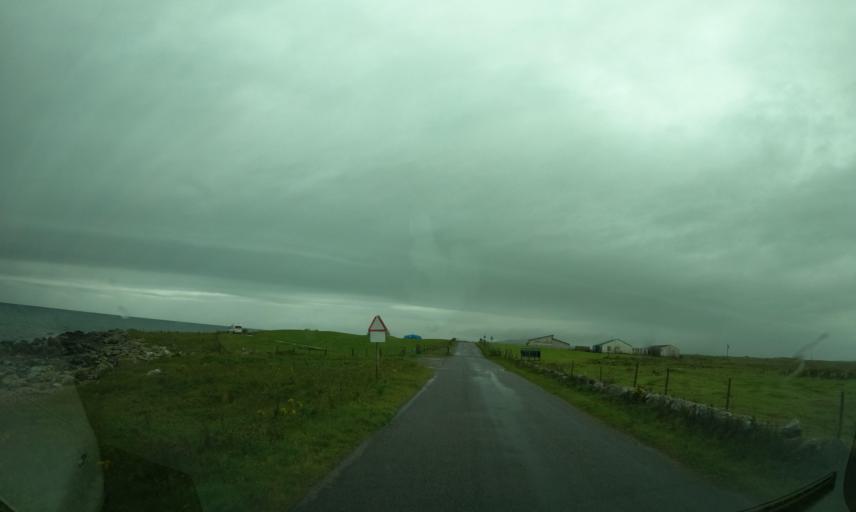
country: GB
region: Scotland
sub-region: Eilean Siar
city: Barra
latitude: 56.4851
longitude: -6.8796
